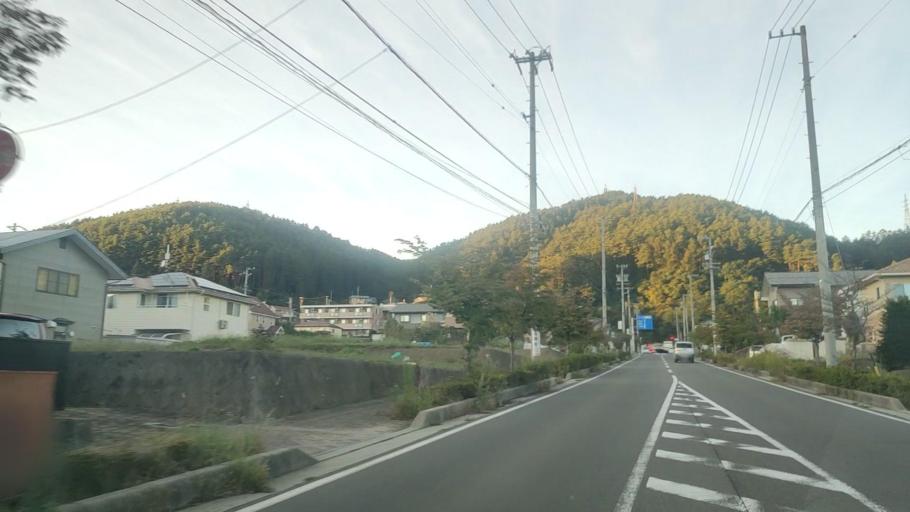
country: JP
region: Nagano
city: Okaya
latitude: 36.0841
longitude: 138.0655
